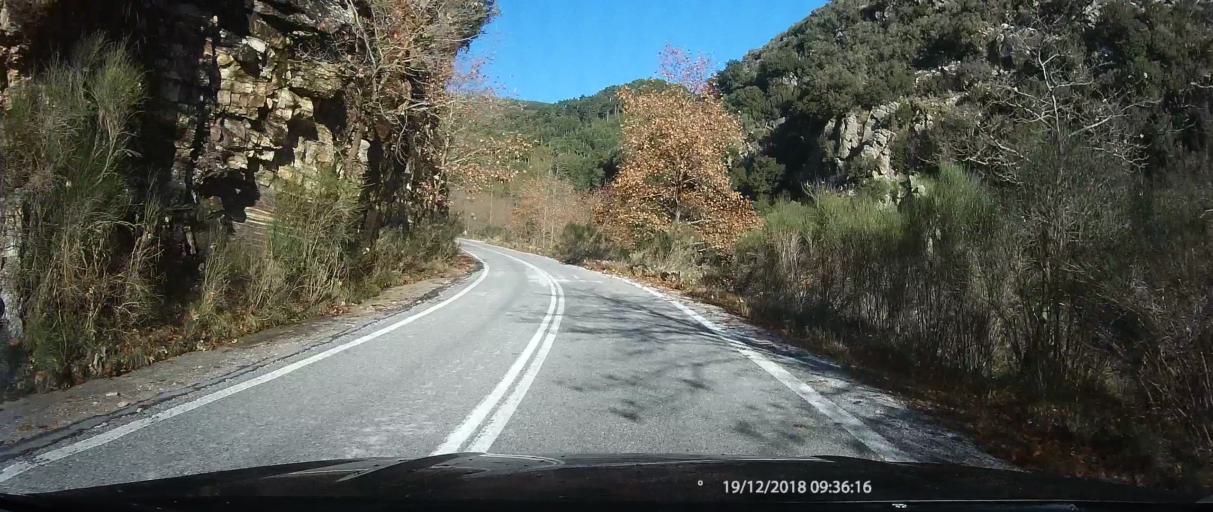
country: GR
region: Peloponnese
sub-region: Nomos Lakonias
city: Magoula
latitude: 37.0811
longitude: 22.2838
